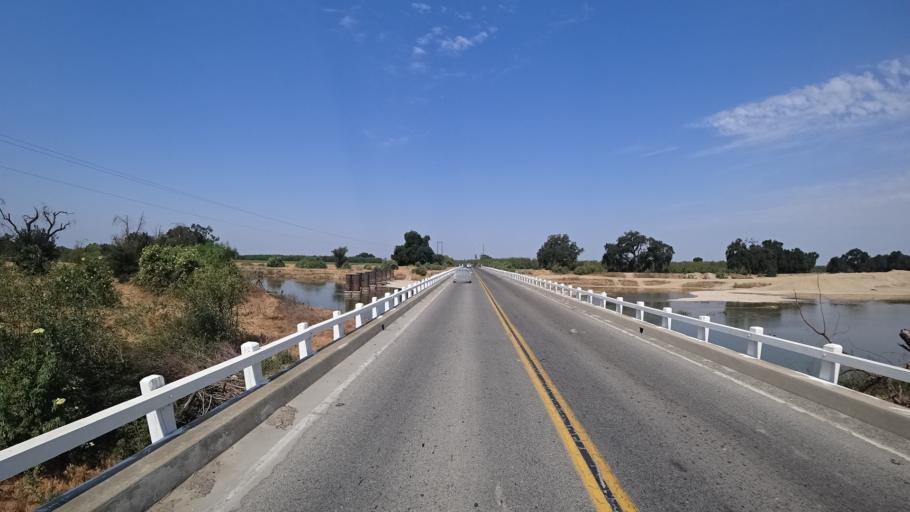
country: US
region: California
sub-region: Fresno County
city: Laton
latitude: 36.4014
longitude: -119.7511
